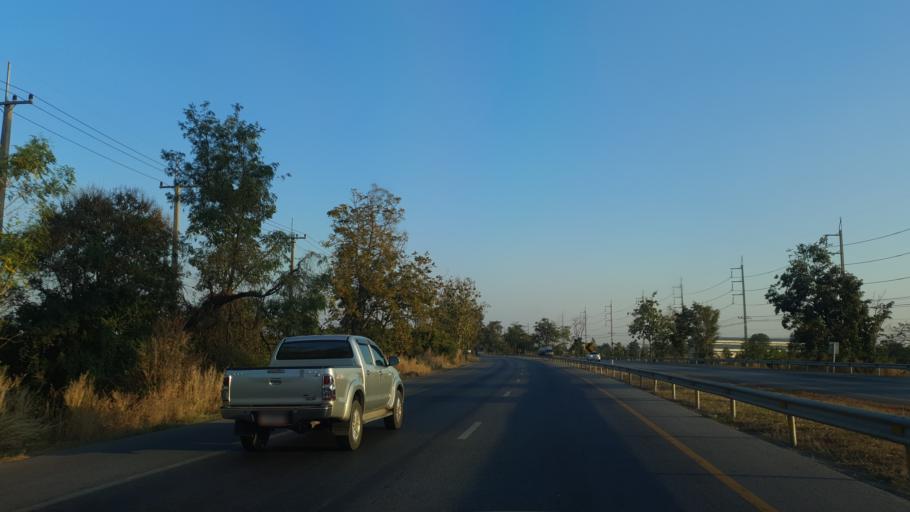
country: TH
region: Kamphaeng Phet
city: Khanu Woralaksaburi
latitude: 16.0652
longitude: 99.7356
